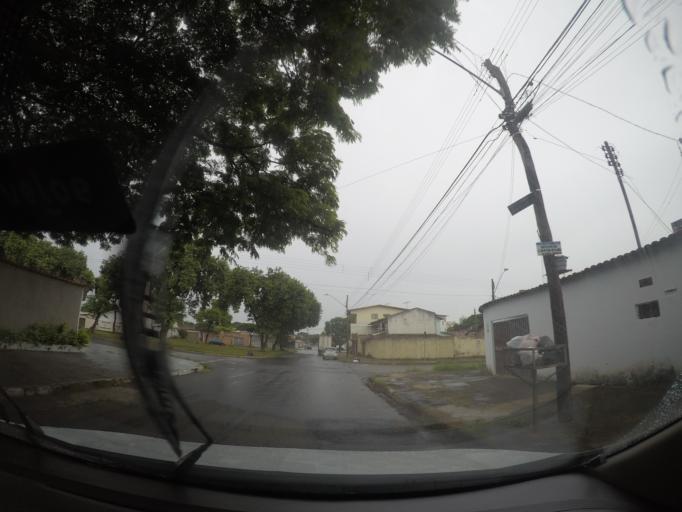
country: BR
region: Goias
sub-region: Goiania
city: Goiania
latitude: -16.7137
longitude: -49.3009
